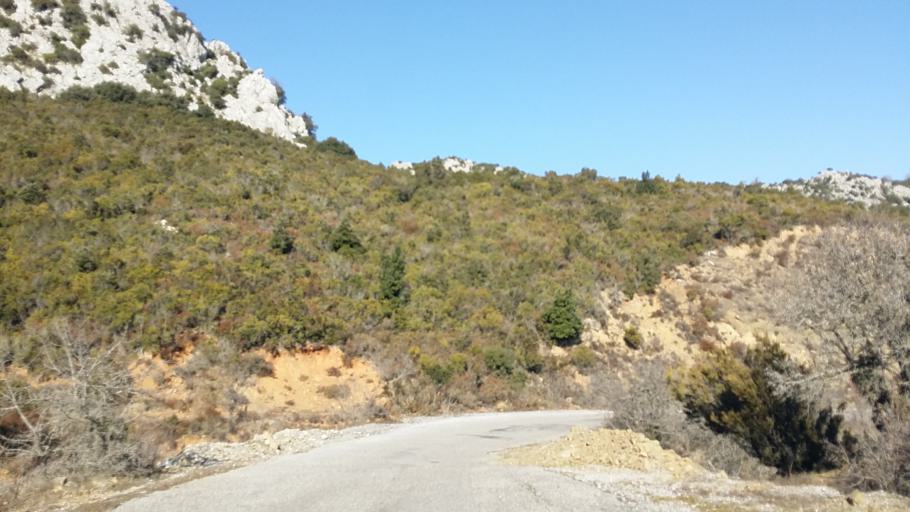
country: GR
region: West Greece
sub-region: Nomos Aitolias kai Akarnanias
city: Sardinia
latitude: 38.9242
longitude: 21.4243
